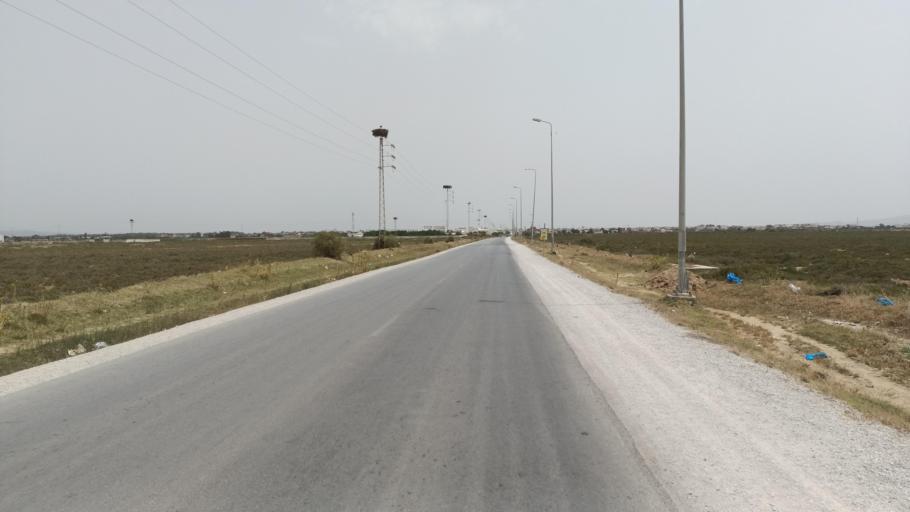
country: TN
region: Nabul
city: Manzil Bu Zalafah
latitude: 36.7177
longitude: 10.4769
